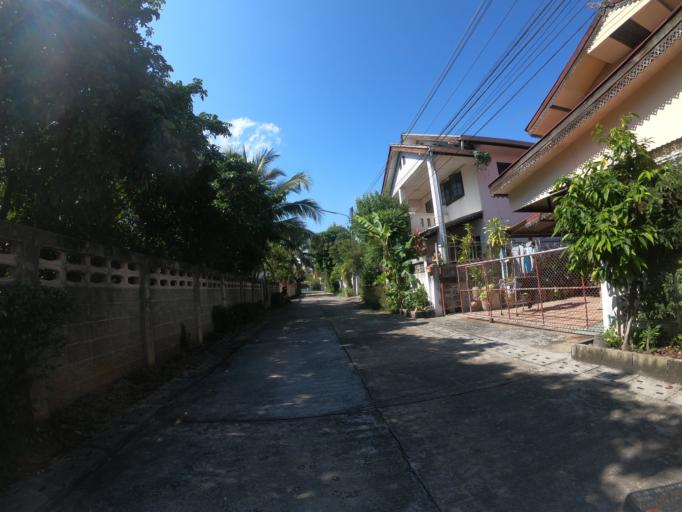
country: TH
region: Chiang Mai
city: Chiang Mai
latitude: 18.7490
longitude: 98.9710
